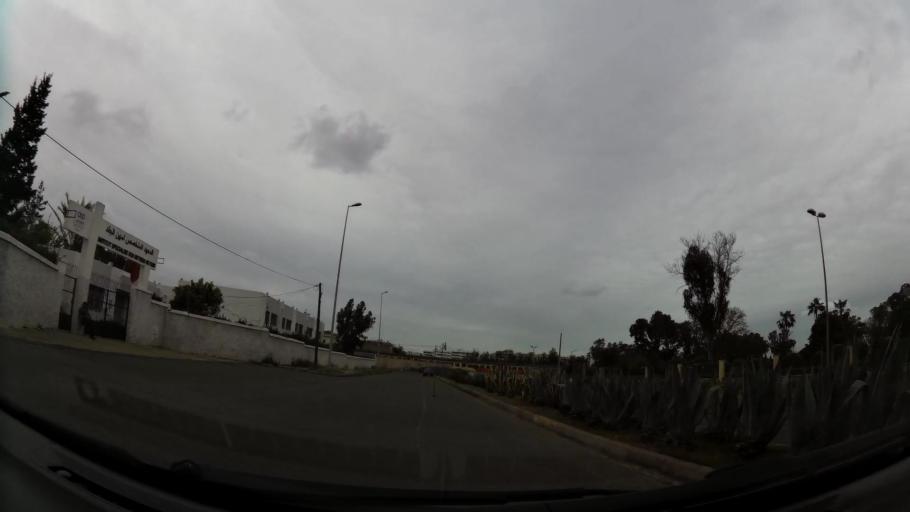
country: MA
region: Grand Casablanca
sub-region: Casablanca
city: Casablanca
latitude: 33.5651
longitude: -7.6149
